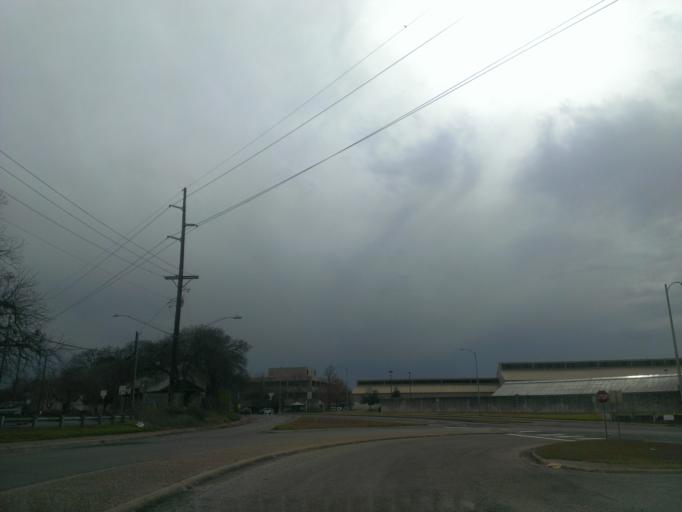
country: US
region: Texas
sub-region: Travis County
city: Austin
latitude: 30.2865
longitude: -97.7237
